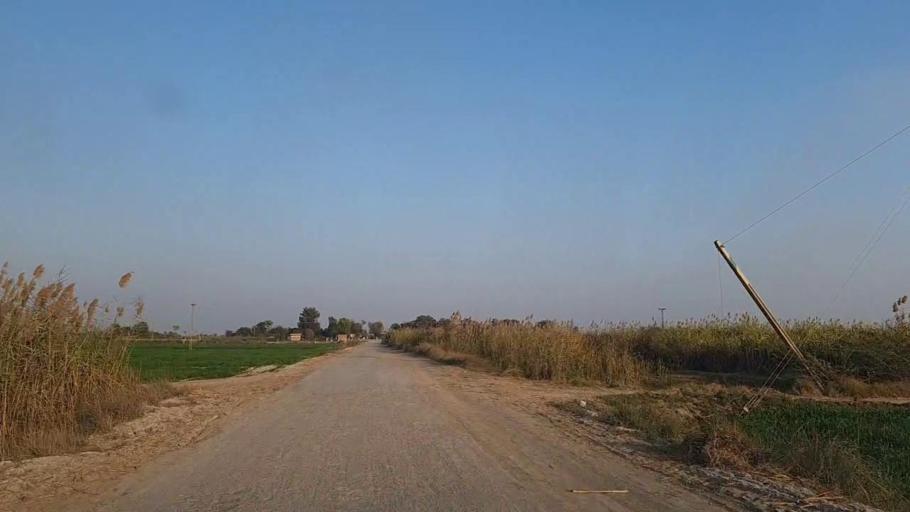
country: PK
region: Sindh
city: Daur
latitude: 26.5105
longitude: 68.3052
